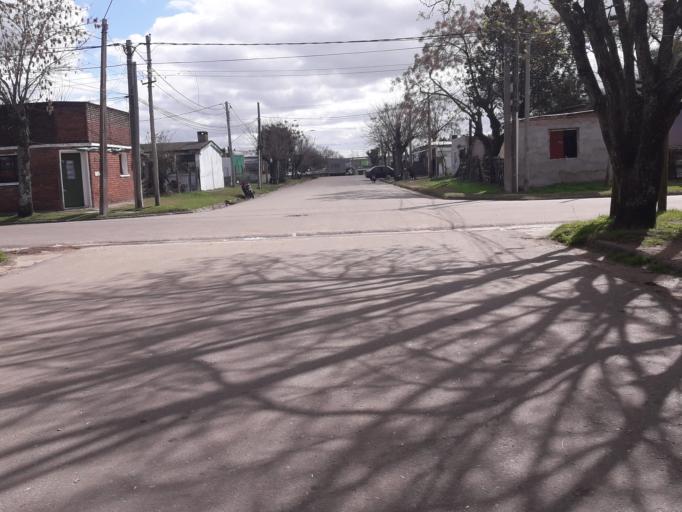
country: UY
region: Durazno
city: Santa Bernardina
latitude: -33.3703
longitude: -56.5299
